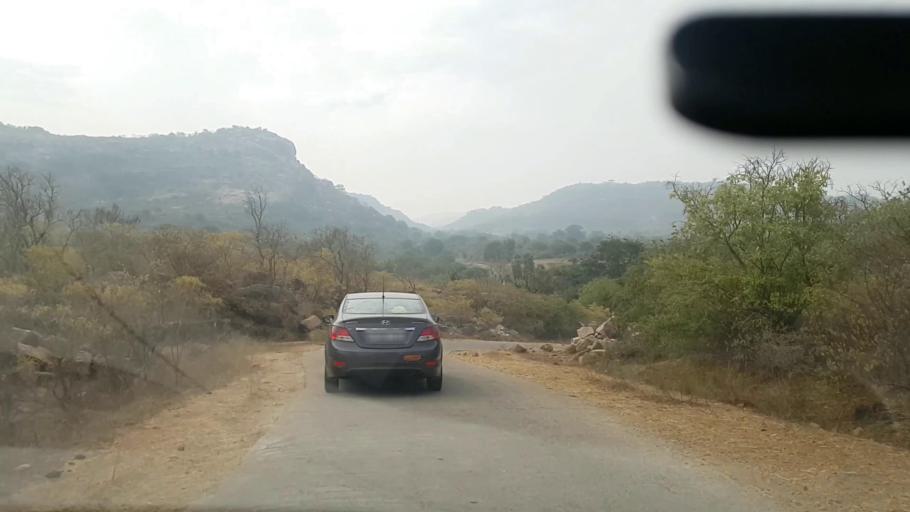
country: IN
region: Telangana
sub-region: Rangareddi
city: Ghatkesar
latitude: 17.1804
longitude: 78.8220
